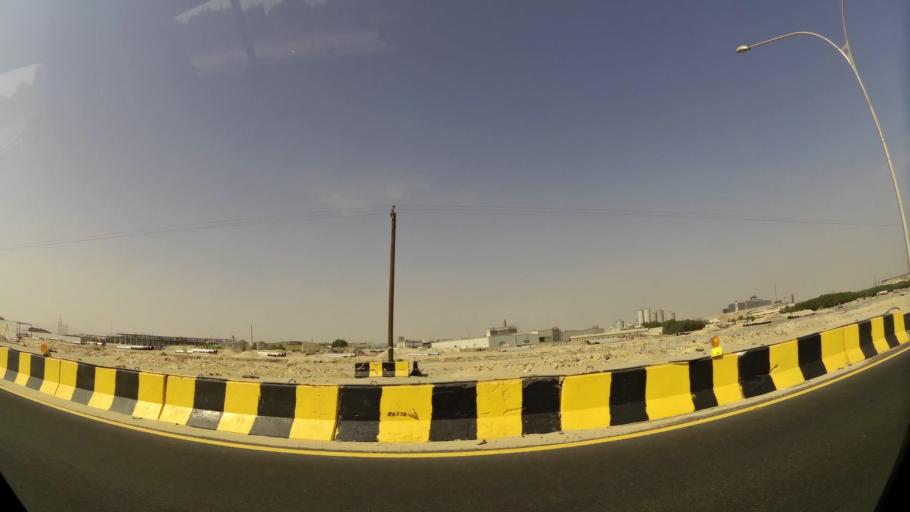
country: KW
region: Al Ahmadi
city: Al Fahahil
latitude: 28.9799
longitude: 48.1332
